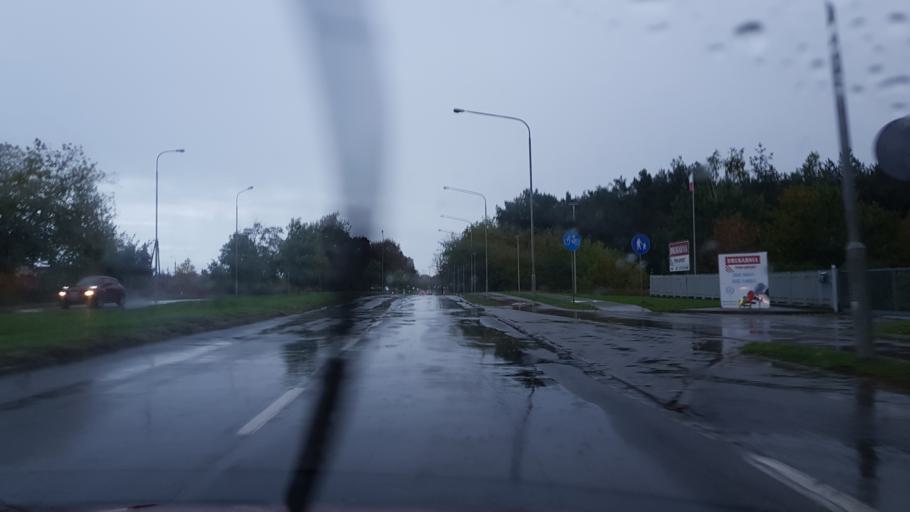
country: PL
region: Greater Poland Voivodeship
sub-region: Powiat pilski
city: Pila
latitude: 53.1536
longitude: 16.6992
